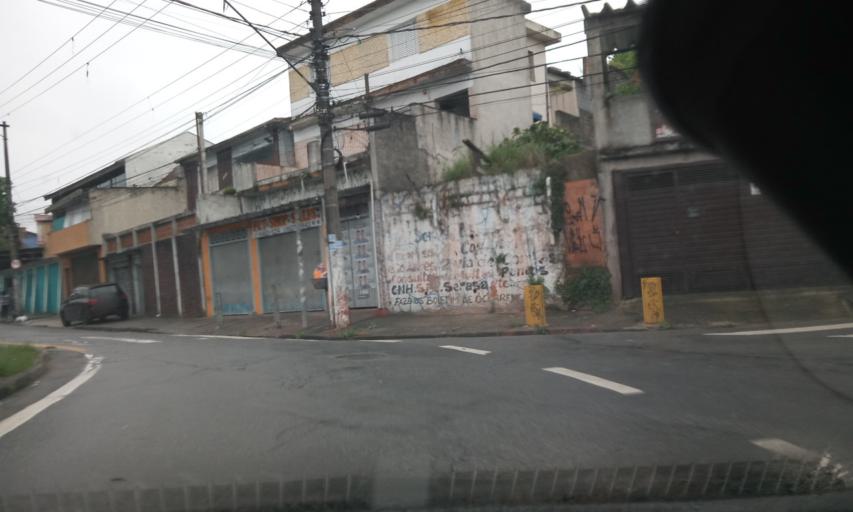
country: BR
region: Sao Paulo
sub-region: Santo Andre
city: Santo Andre
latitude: -23.6998
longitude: -46.5166
